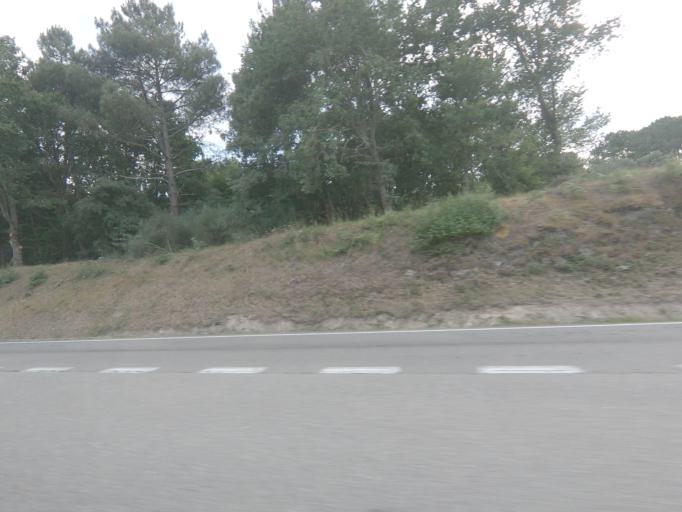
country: ES
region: Galicia
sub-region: Provincia de Ourense
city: Taboadela
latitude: 42.2177
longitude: -7.8349
